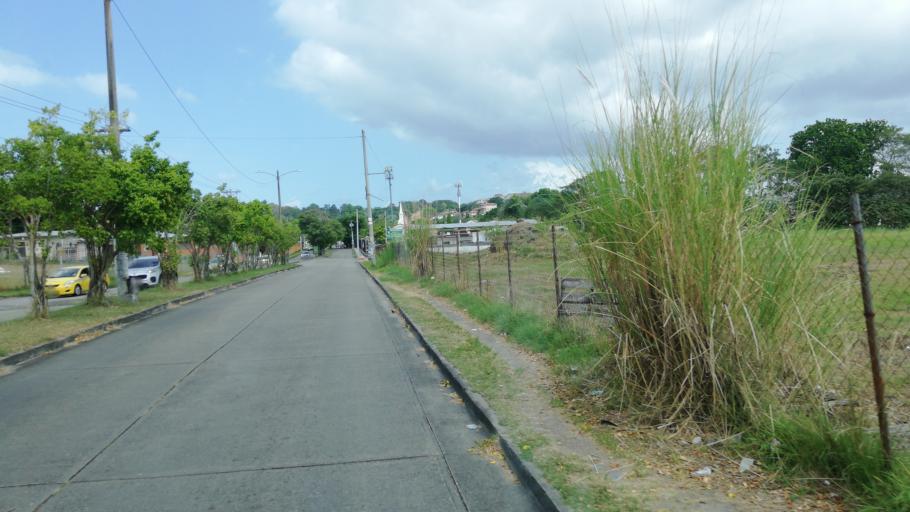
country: PA
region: Panama
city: San Miguelito
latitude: 9.0556
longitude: -79.4596
